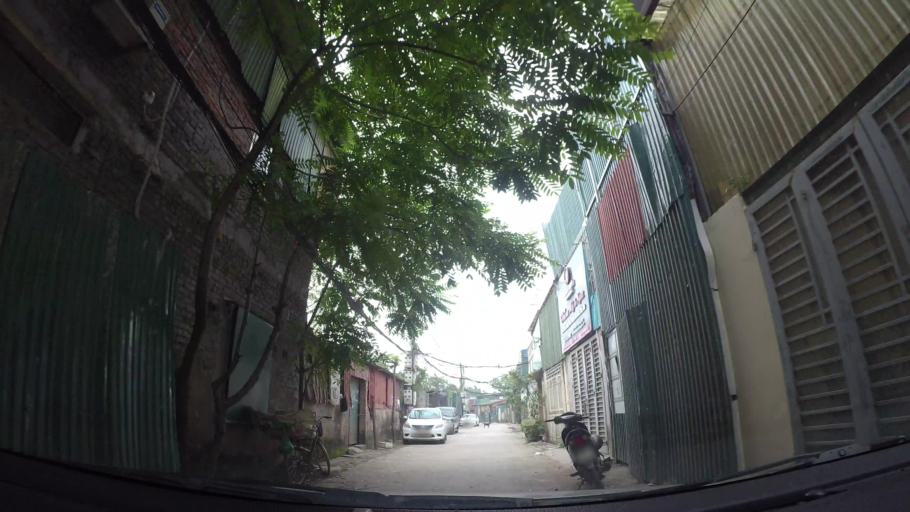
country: VN
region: Ha Noi
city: Tay Ho
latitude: 21.0685
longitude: 105.8299
